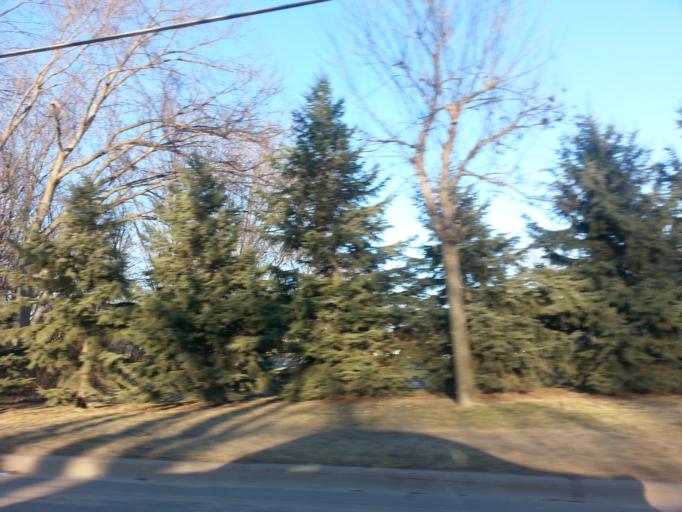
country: US
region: Minnesota
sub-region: Washington County
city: Oak Park Heights
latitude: 45.0316
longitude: -92.8073
